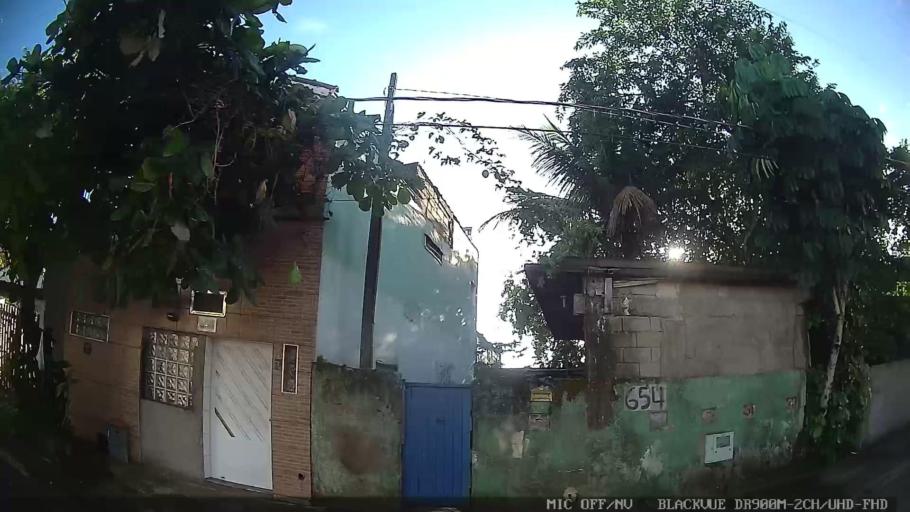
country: BR
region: Sao Paulo
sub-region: Itanhaem
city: Itanhaem
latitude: -24.2430
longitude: -46.8953
